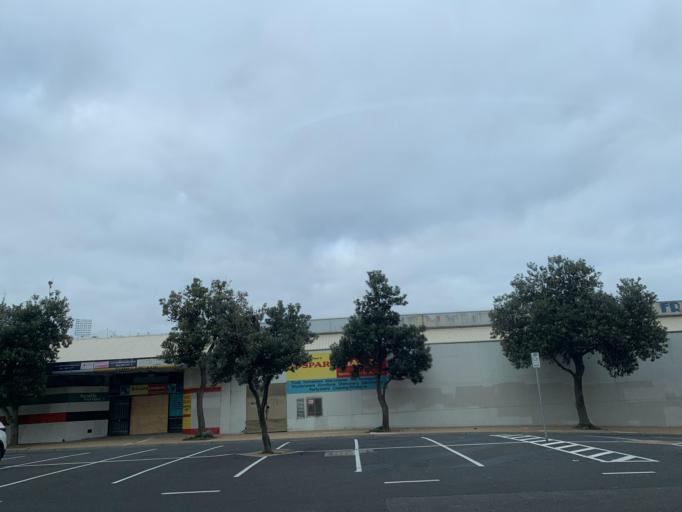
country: AU
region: Victoria
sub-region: Frankston
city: Frankston
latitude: -38.1437
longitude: 145.1202
